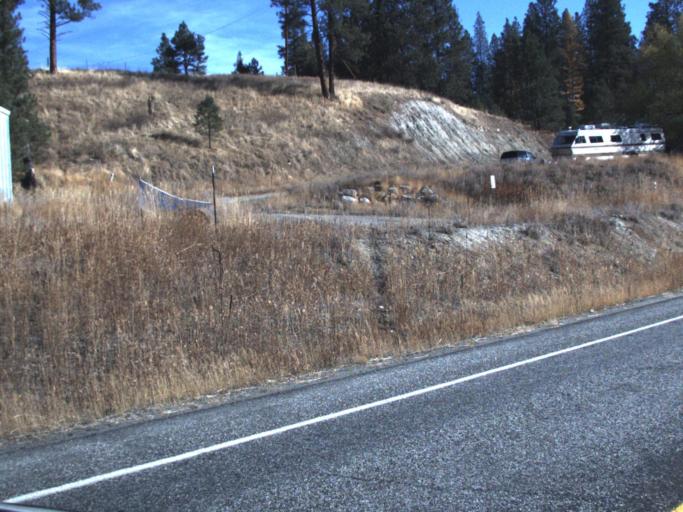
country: US
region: Washington
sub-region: Ferry County
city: Republic
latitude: 48.6496
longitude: -118.7774
